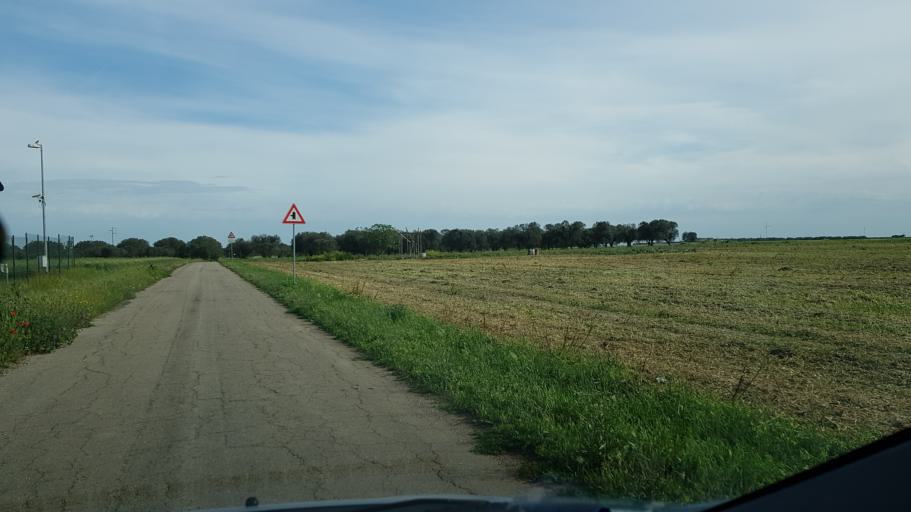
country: IT
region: Apulia
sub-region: Provincia di Brindisi
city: Tuturano
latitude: 40.5248
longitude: 17.9689
